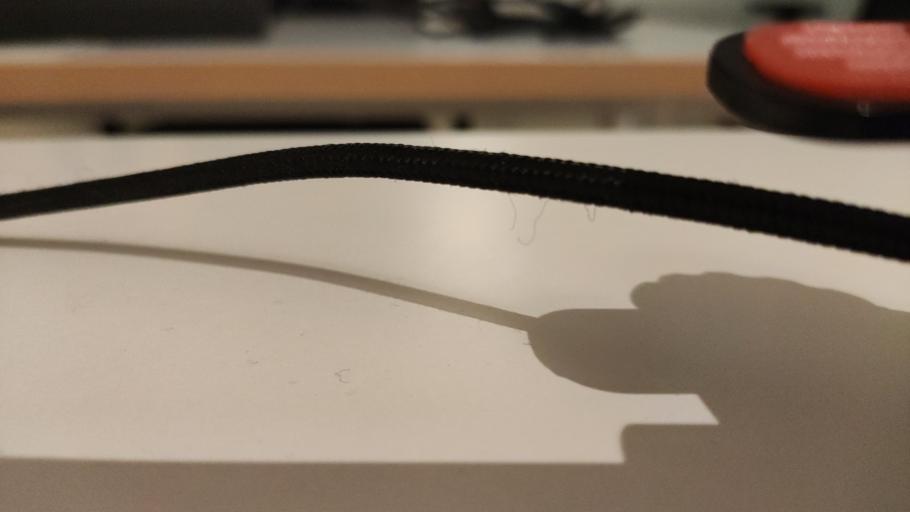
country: RU
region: Moskovskaya
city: Shaburnovo
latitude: 56.4310
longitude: 37.9403
